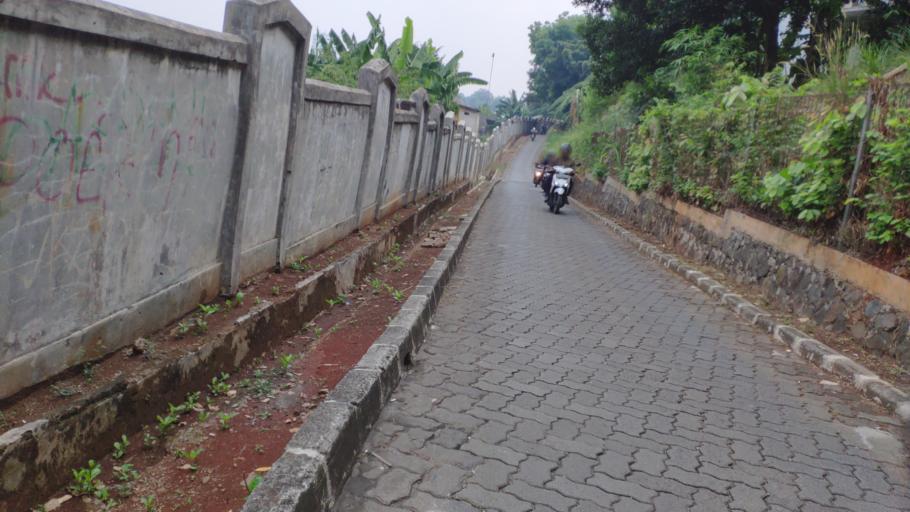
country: ID
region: Jakarta Raya
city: Jakarta
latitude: -6.3053
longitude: 106.8243
